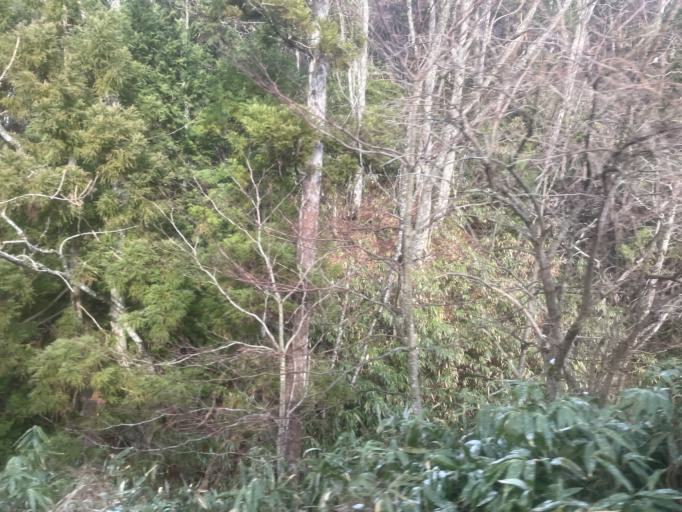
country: JP
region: Aomori
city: Goshogawara
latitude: 41.0798
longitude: 140.5269
